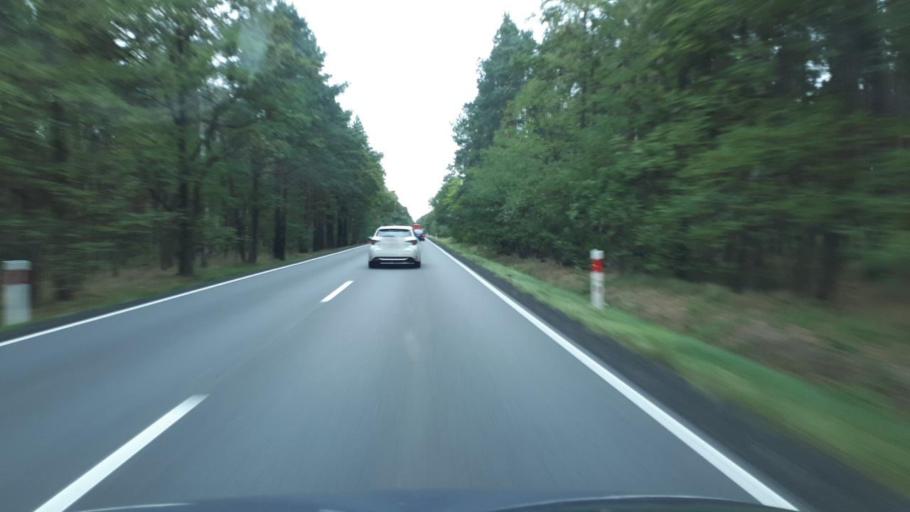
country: PL
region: Greater Poland Voivodeship
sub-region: Powiat ostrowski
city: Przygodzice
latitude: 51.4953
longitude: 17.8548
